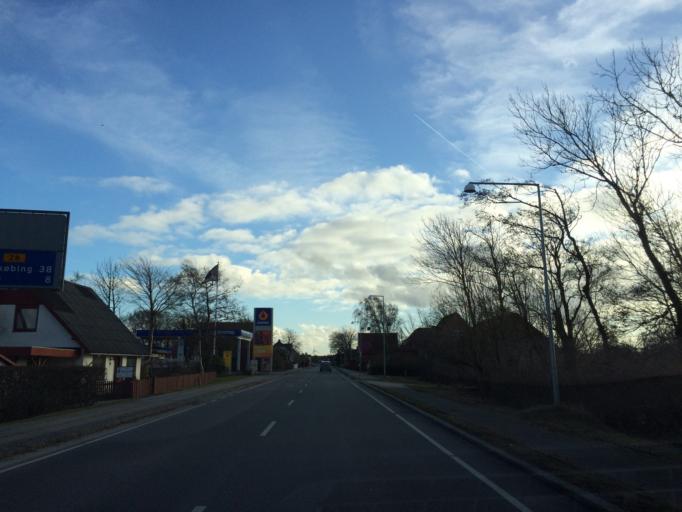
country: DK
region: Central Jutland
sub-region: Lemvig Kommune
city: Lemvig
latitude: 56.4176
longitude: 8.3072
